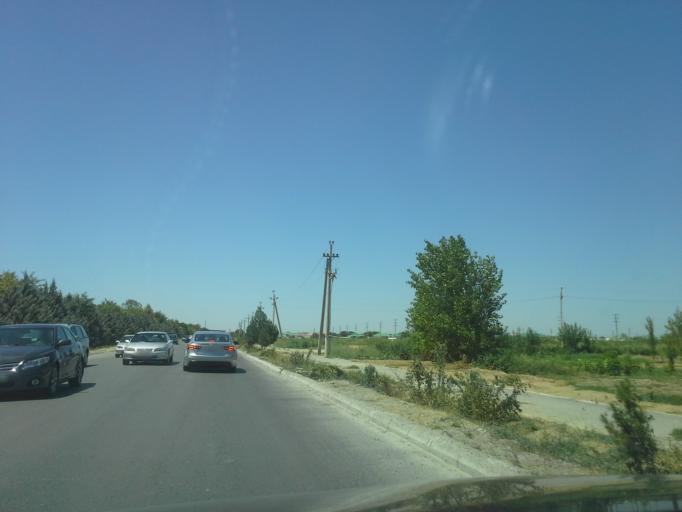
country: TM
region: Ahal
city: Abadan
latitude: 38.0290
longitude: 58.2352
